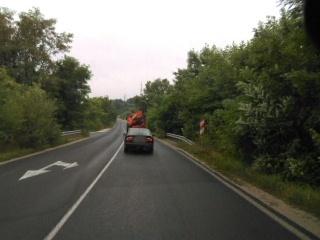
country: BG
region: Plovdiv
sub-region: Obshtina Karlovo
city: Karlovo
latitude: 42.5367
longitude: 24.8171
